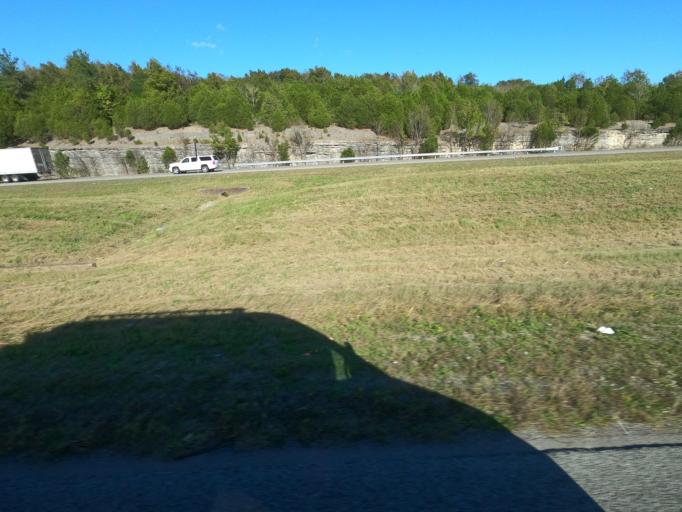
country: US
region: Tennessee
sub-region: Rutherford County
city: Plainview
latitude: 35.6930
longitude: -86.2995
